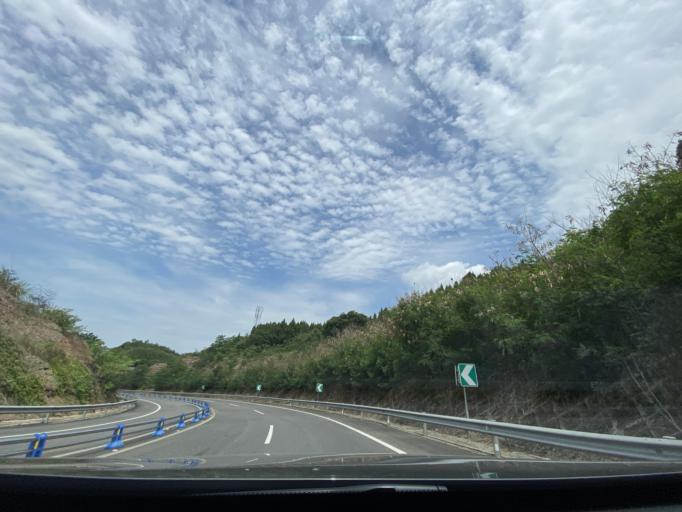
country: CN
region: Sichuan
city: Mianyang
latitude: 31.3493
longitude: 104.7073
